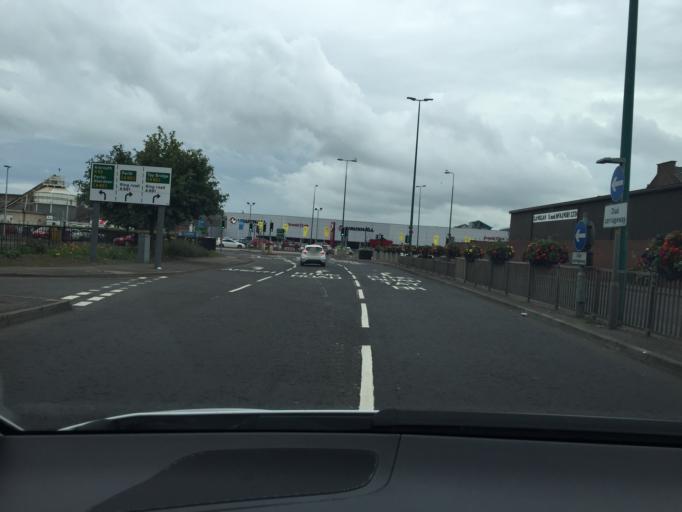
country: GB
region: Scotland
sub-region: Dundee City
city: Dundee
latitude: 56.4633
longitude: -2.9635
